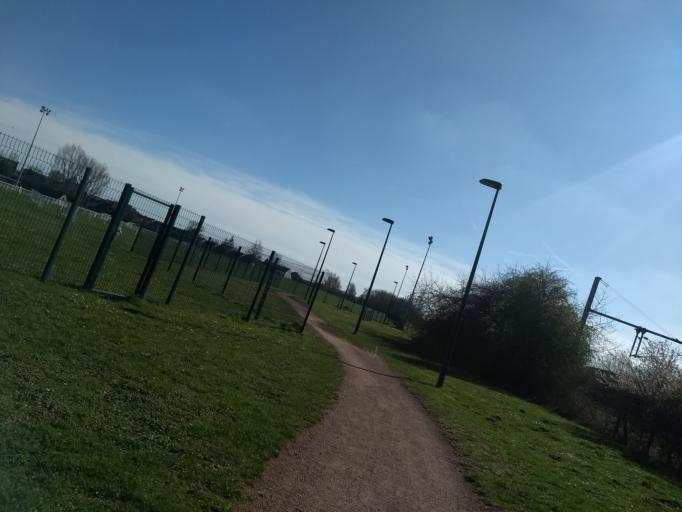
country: FR
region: Nord-Pas-de-Calais
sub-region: Departement du Pas-de-Calais
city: Achicourt
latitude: 50.2707
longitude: 2.7642
